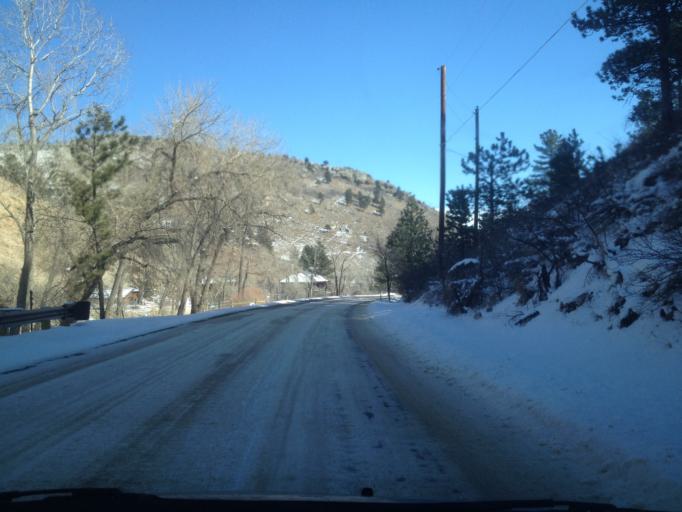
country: US
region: Colorado
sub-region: Boulder County
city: Boulder
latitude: 40.0644
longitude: -105.3054
